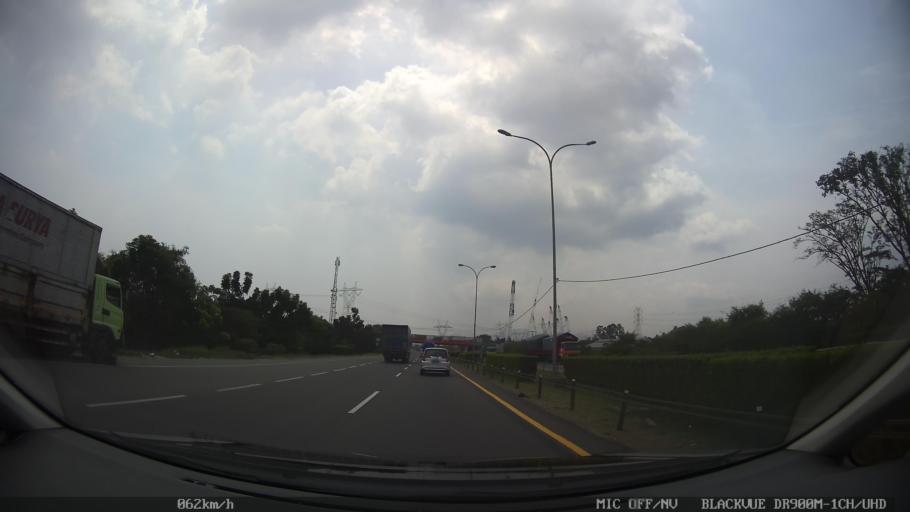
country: ID
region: Banten
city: Bojonegara
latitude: -6.0189
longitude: 106.0892
